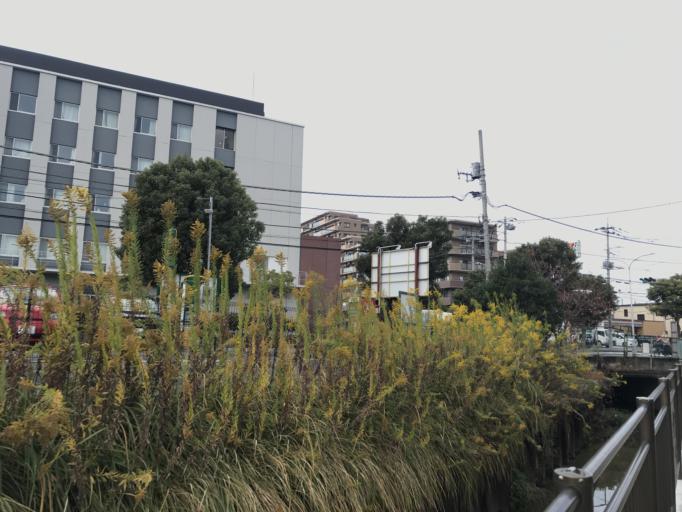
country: JP
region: Chiba
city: Funabashi
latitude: 35.7126
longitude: 139.9842
